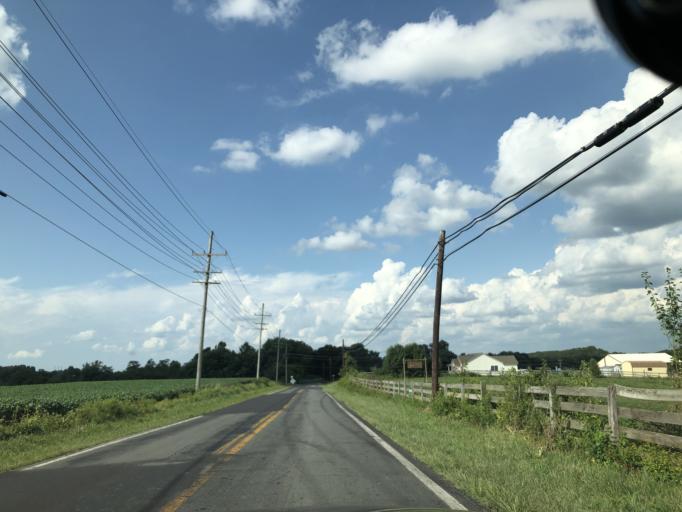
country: US
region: Maryland
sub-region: Carroll County
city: Mount Airy
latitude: 39.3981
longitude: -77.1797
